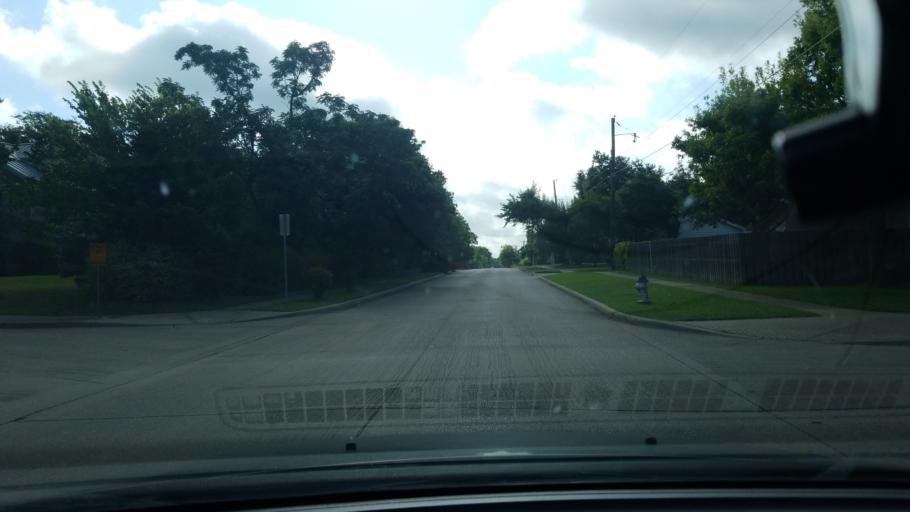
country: US
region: Texas
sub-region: Dallas County
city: Garland
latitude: 32.8218
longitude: -96.6887
